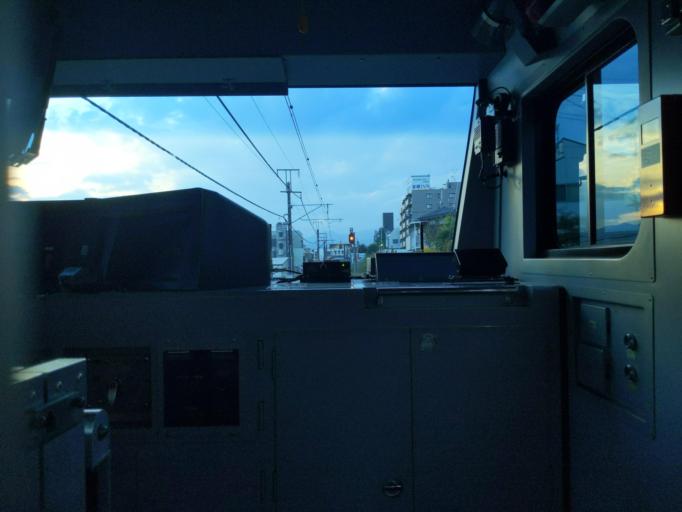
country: JP
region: Tokyo
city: Fussa
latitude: 35.7276
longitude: 139.2901
